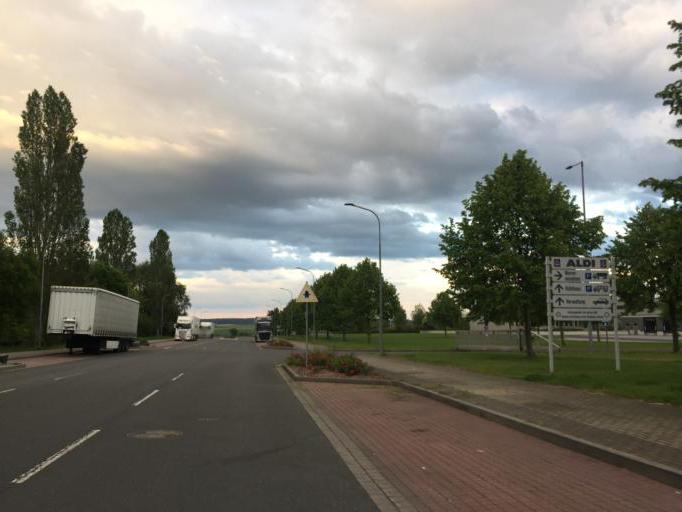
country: DE
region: Hesse
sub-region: Regierungsbezirk Darmstadt
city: Butzbach
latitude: 50.4289
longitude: 8.6885
